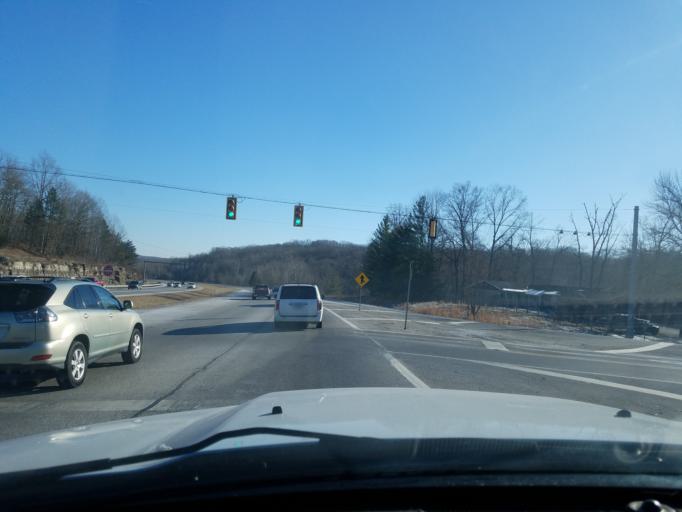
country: US
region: Indiana
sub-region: Lawrence County
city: Oolitic
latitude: 38.9099
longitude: -86.5453
